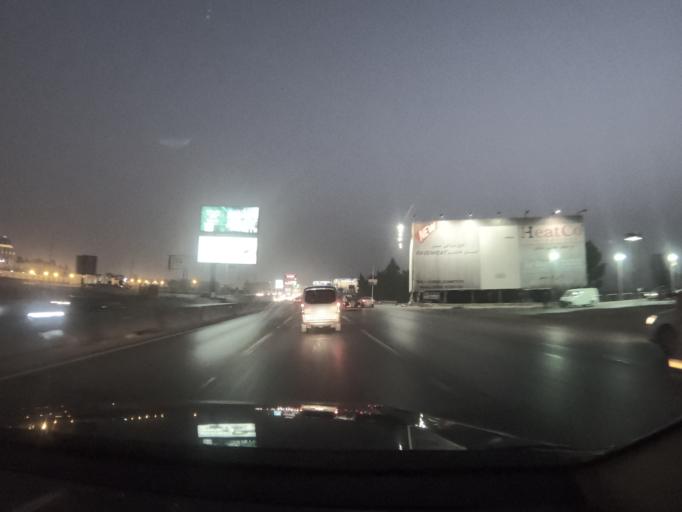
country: EG
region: Muhafazat al Qalyubiyah
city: Al Khankah
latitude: 30.0627
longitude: 31.4185
